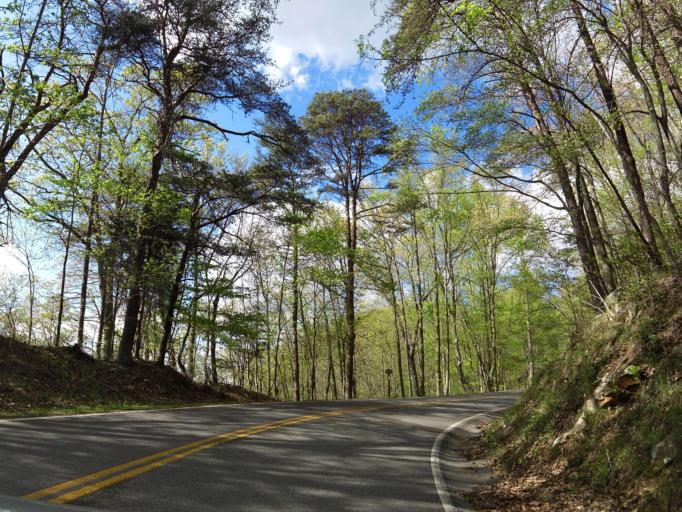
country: US
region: Tennessee
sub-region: Claiborne County
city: Harrogate
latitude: 36.6093
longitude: -83.6741
